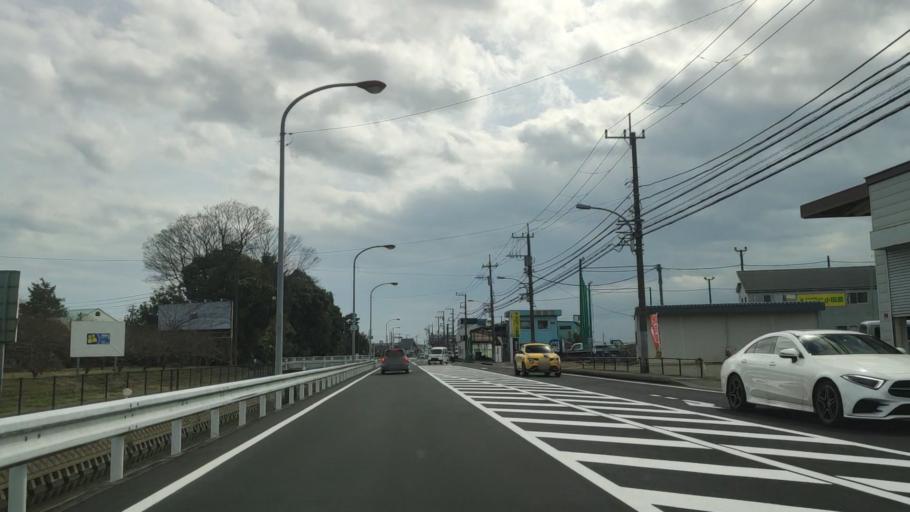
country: JP
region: Kanagawa
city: Odawara
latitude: 35.3082
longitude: 139.1646
